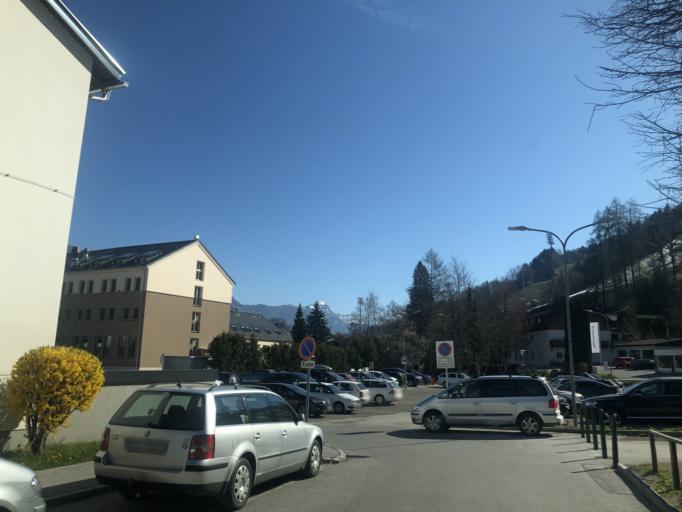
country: AT
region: Styria
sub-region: Politischer Bezirk Liezen
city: Schladming
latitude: 47.3914
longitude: 13.6904
